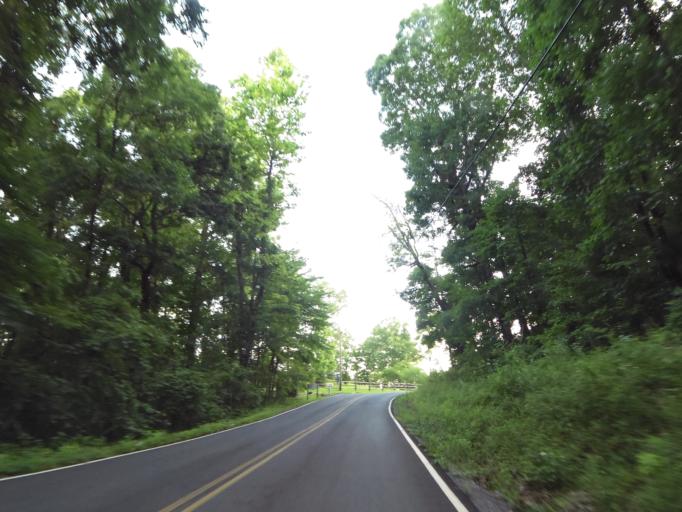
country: US
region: Tennessee
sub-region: Blount County
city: Maryville
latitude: 35.6322
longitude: -83.9370
